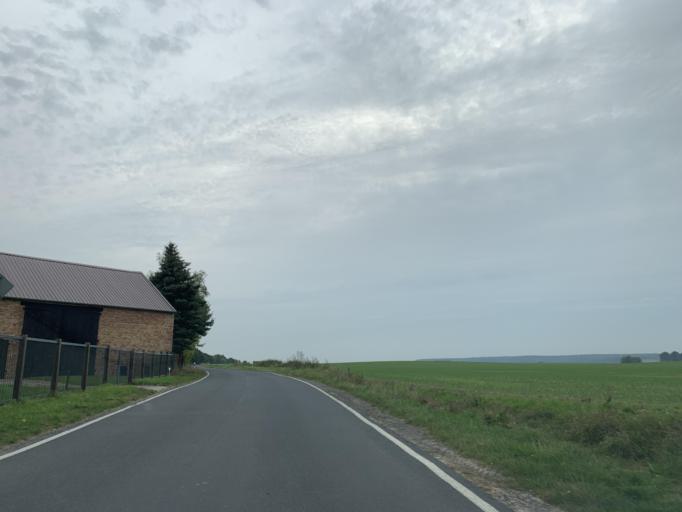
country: DE
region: Brandenburg
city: Mittenwalde
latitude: 53.3269
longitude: 13.7019
